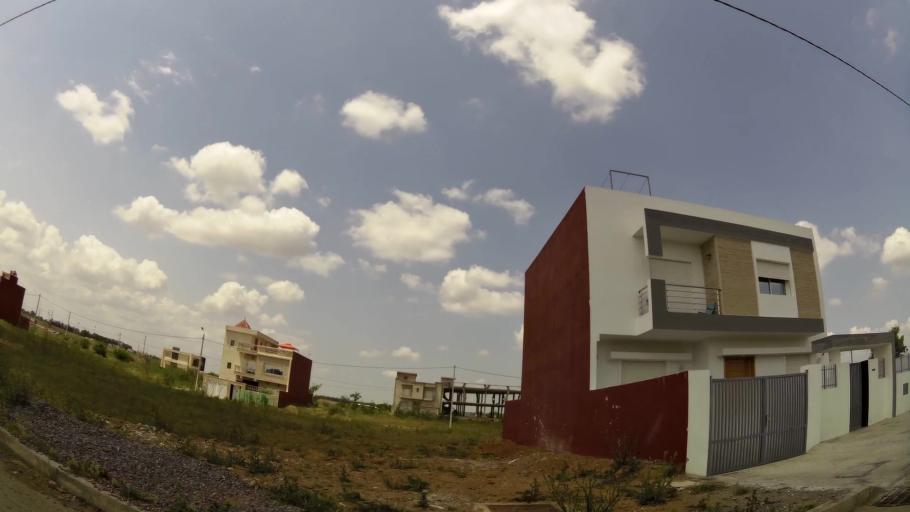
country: MA
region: Gharb-Chrarda-Beni Hssen
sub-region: Kenitra Province
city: Kenitra
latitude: 34.0050
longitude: -6.5410
